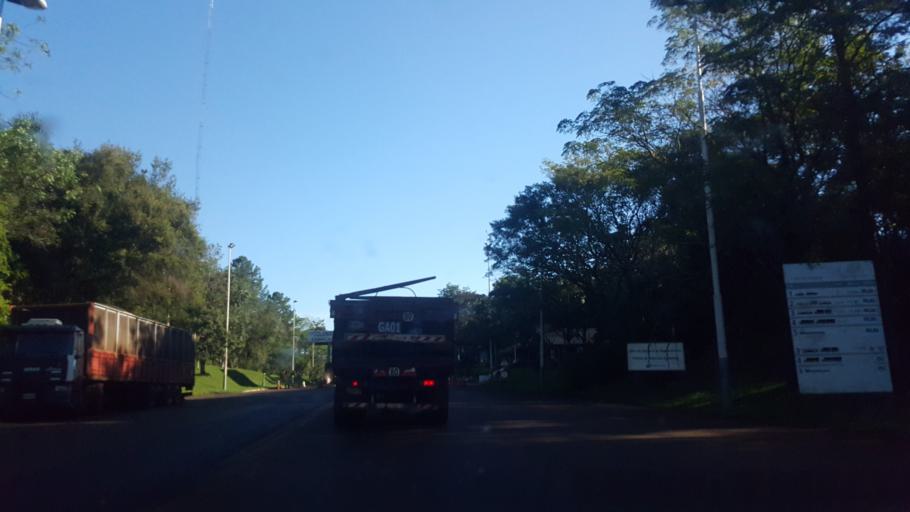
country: AR
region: Misiones
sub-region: Departamento de Eldorado
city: Eldorado
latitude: -26.3353
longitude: -54.6173
